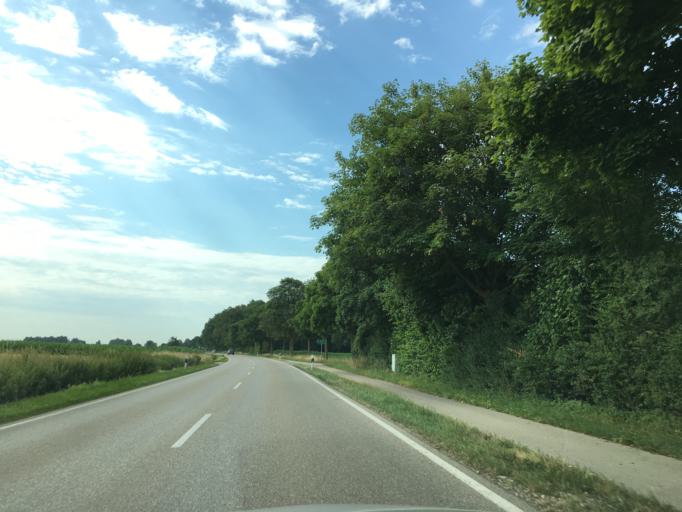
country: DE
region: Bavaria
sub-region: Upper Bavaria
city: Worth
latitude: 48.2659
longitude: 11.9232
